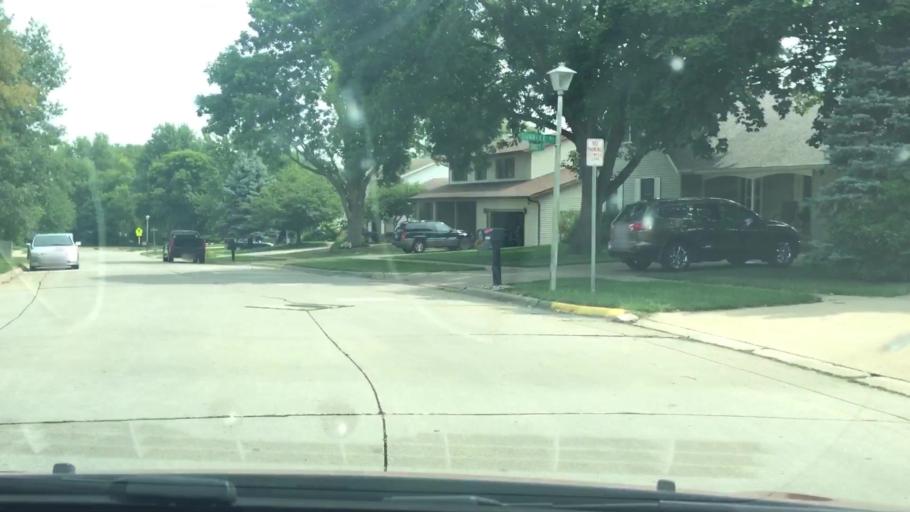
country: US
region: Iowa
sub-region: Muscatine County
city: Muscatine
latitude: 41.4403
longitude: -91.0572
